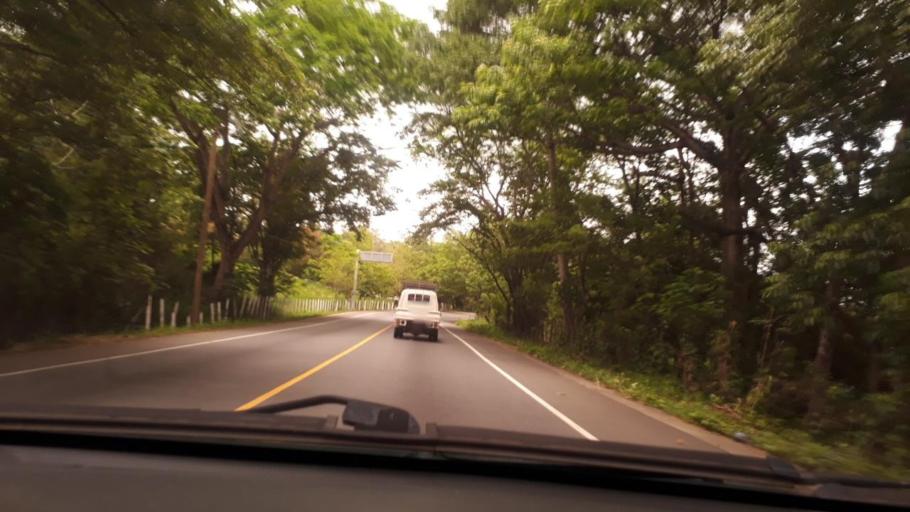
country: GT
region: Izabal
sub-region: Municipio de Los Amates
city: Los Amates
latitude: 15.2332
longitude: -89.2026
